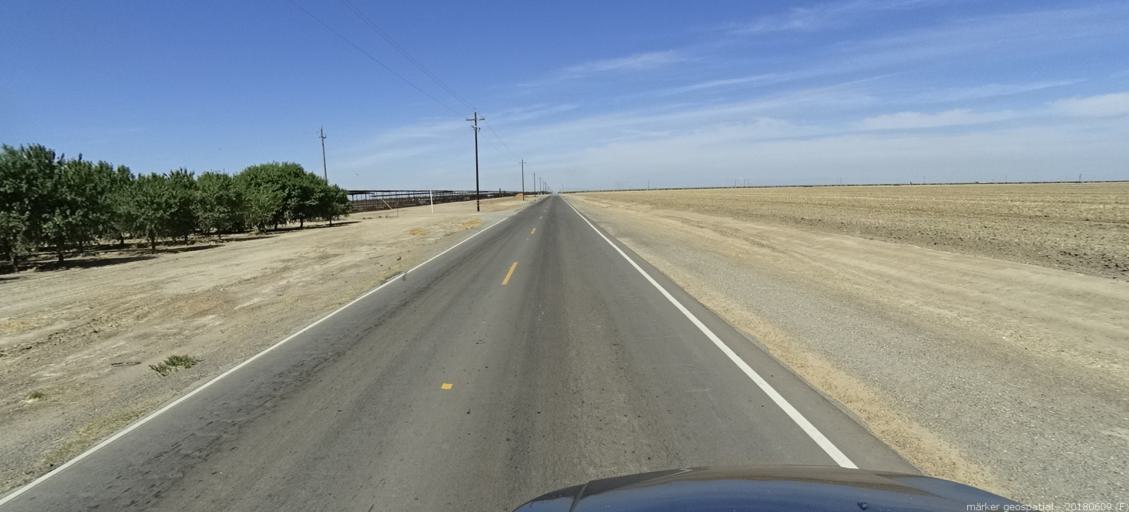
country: US
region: California
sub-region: Madera County
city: Fairmead
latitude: 36.9528
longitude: -120.3031
